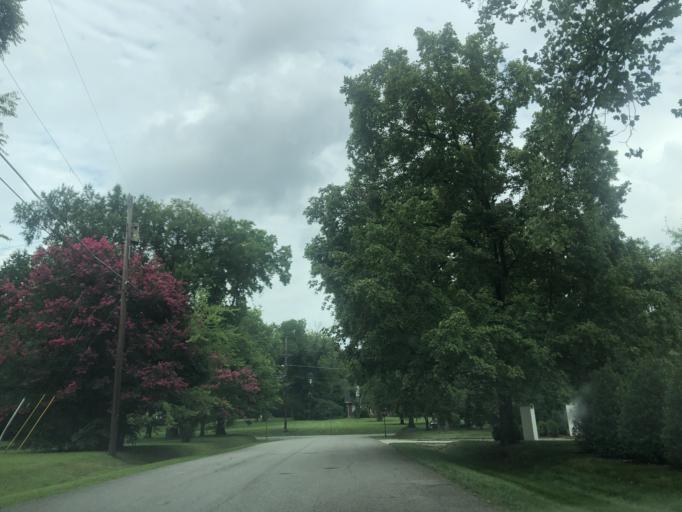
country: US
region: Tennessee
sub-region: Davidson County
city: Oak Hill
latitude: 36.0873
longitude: -86.7857
